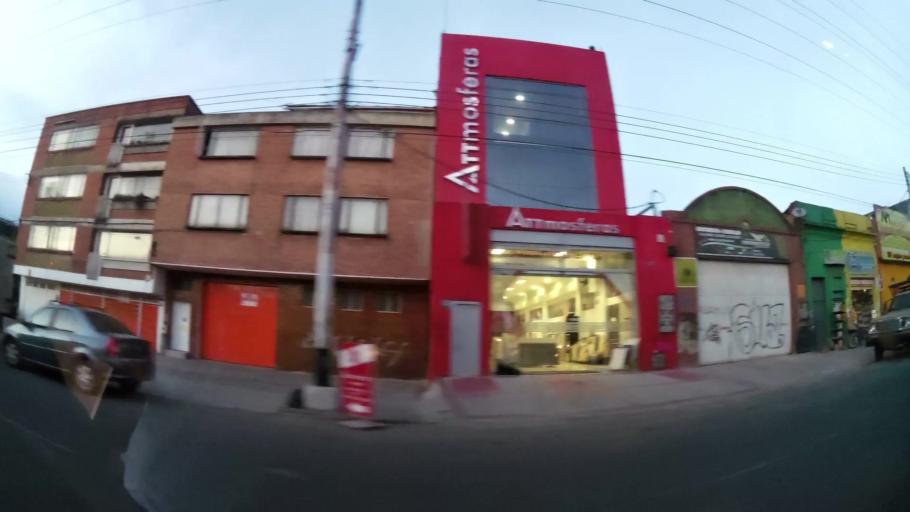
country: CO
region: Bogota D.C.
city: Barrio San Luis
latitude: 4.6574
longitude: -74.0673
